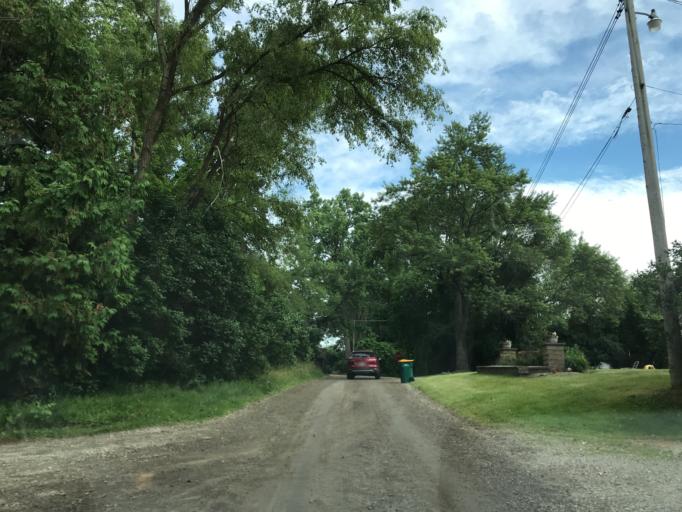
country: US
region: Michigan
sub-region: Oakland County
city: Farmington
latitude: 42.4450
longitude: -83.3414
